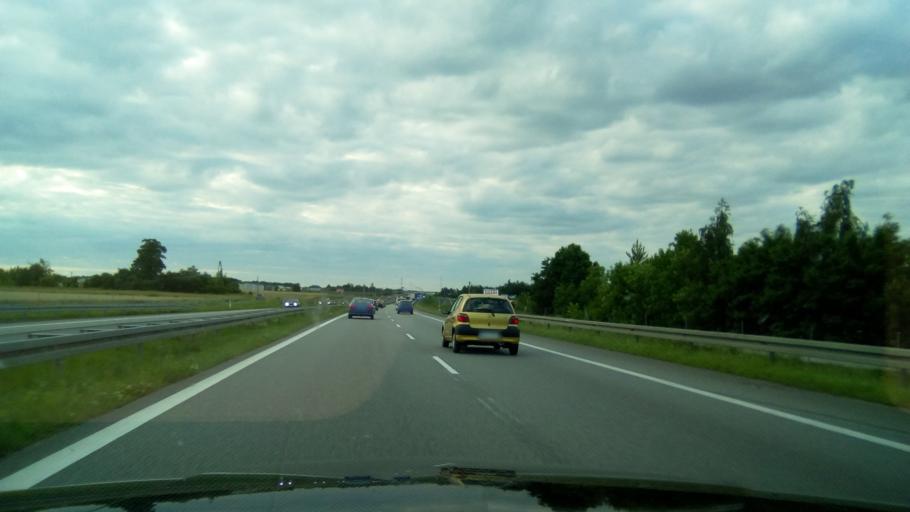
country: PL
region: Masovian Voivodeship
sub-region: Powiat bialobrzeski
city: Promna
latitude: 51.6843
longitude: 20.9367
